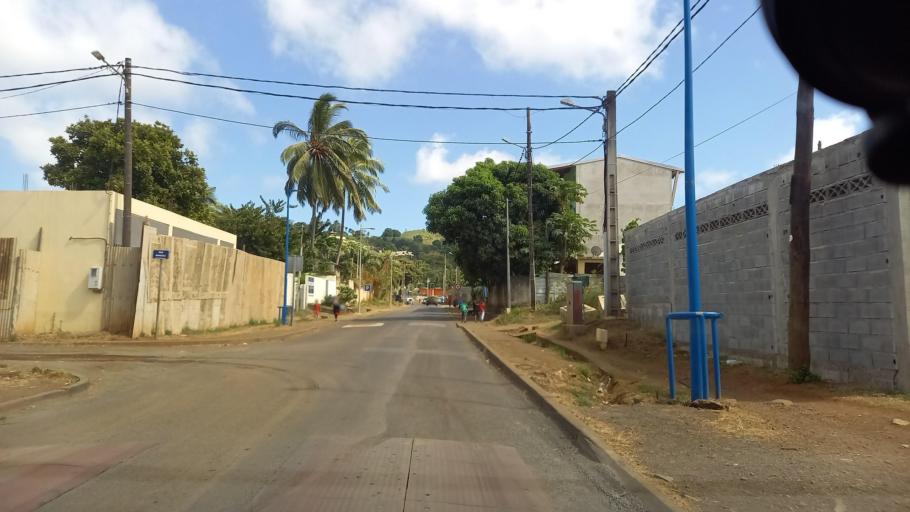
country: YT
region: Mamoudzou
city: Mamoudzou
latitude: -12.8010
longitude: 45.2080
